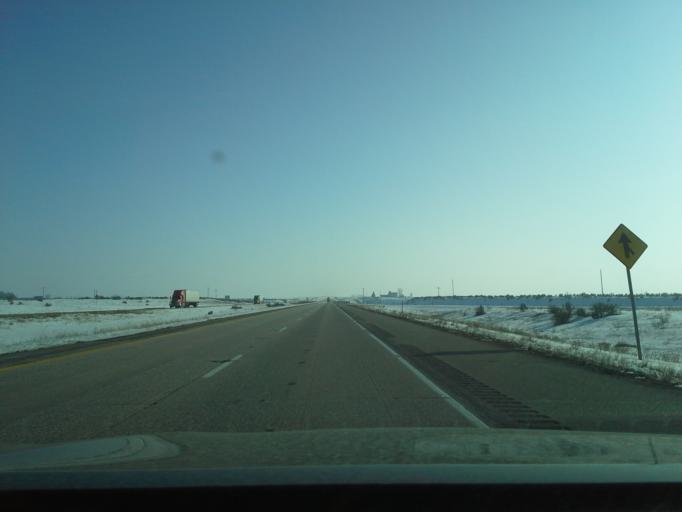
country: US
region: Idaho
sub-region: Oneida County
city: Malad City
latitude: 42.5006
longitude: -112.1697
